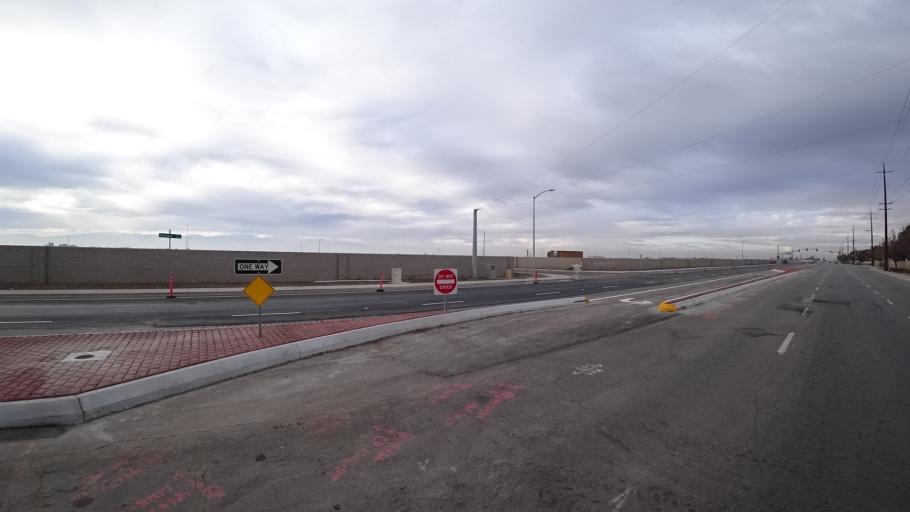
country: US
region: California
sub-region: Kern County
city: Greenfield
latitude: 35.2961
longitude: -119.0806
